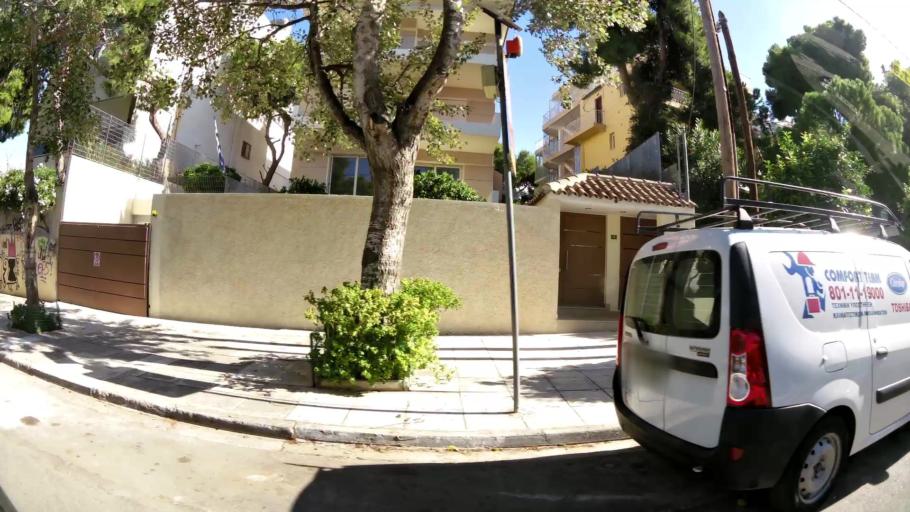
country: GR
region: Attica
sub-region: Nomarchia Anatolikis Attikis
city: Vouliagmeni
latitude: 37.8158
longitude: 23.7820
